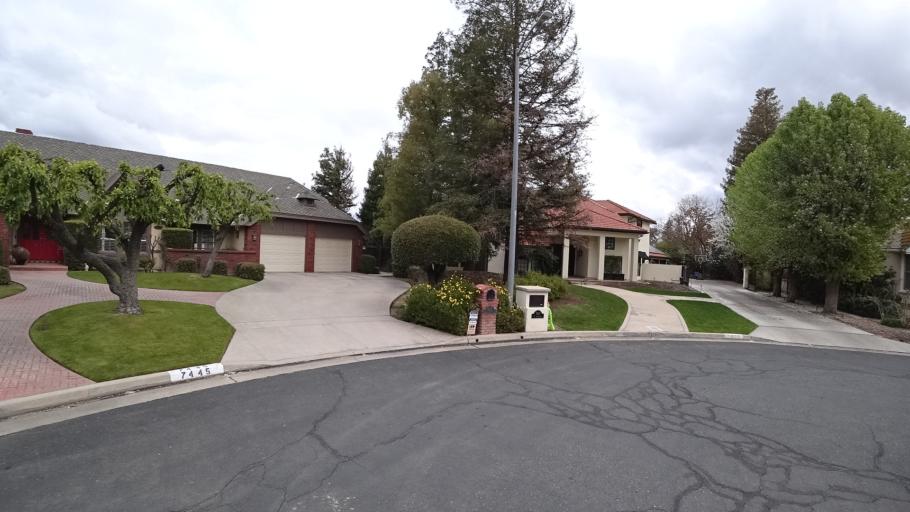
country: US
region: California
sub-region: Fresno County
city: Fresno
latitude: 36.8452
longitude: -119.8391
